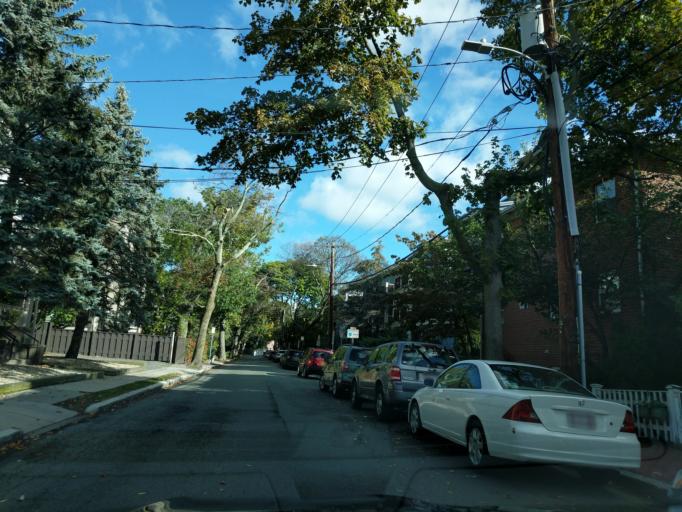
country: US
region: Massachusetts
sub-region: Middlesex County
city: Cambridge
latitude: 42.3762
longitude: -71.1098
